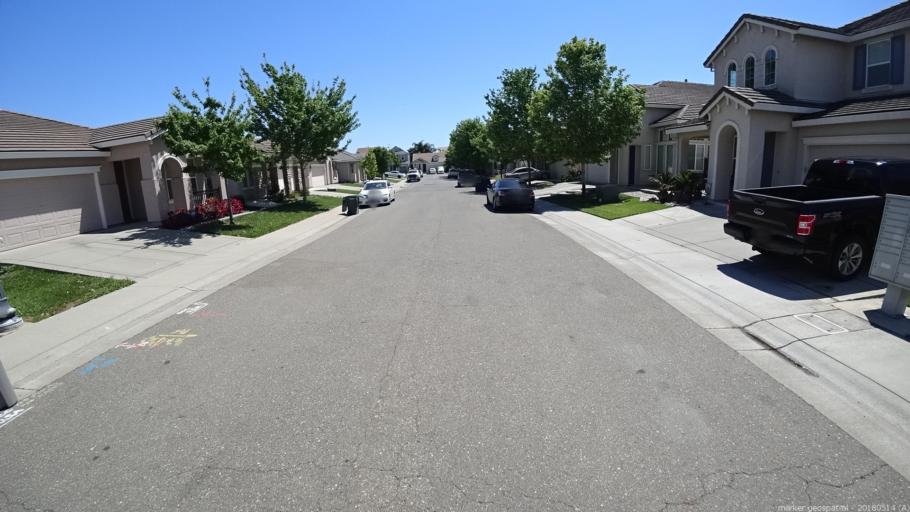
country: US
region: California
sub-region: Yolo County
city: West Sacramento
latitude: 38.6255
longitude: -121.5259
